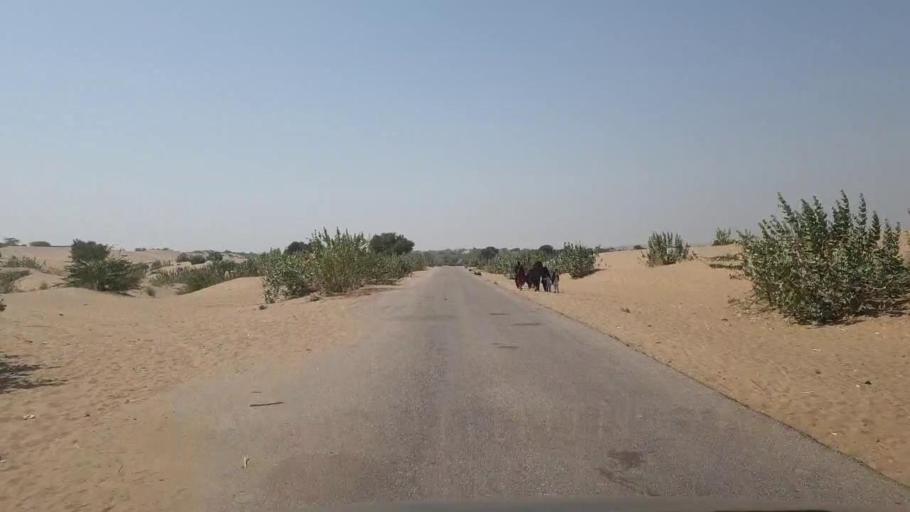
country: PK
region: Sindh
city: Chor
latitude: 25.5756
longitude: 70.1887
